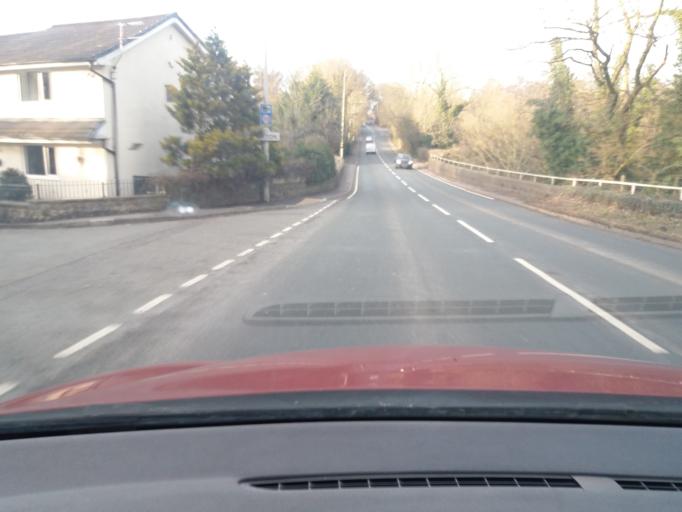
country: GB
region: England
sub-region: Lancashire
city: Euxton
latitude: 53.6546
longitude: -2.6755
